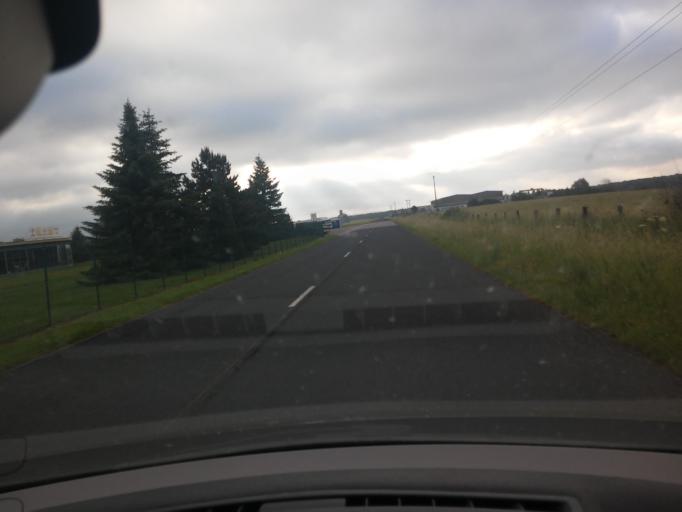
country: FR
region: Lorraine
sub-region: Departement de la Meuse
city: Vigneulles-les-Hattonchatel
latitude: 48.9787
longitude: 5.7269
